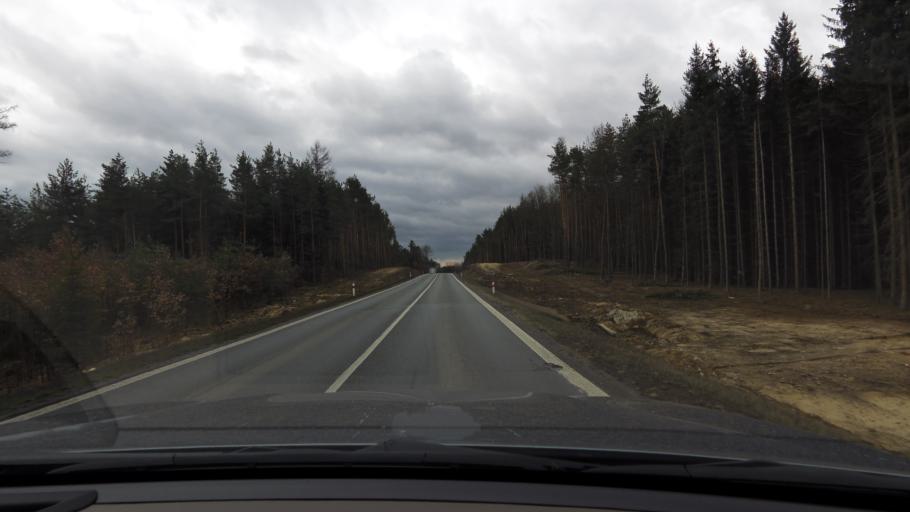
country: CZ
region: Plzensky
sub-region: Okres Plzen-Sever
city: Tremosna
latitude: 49.7958
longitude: 13.3861
